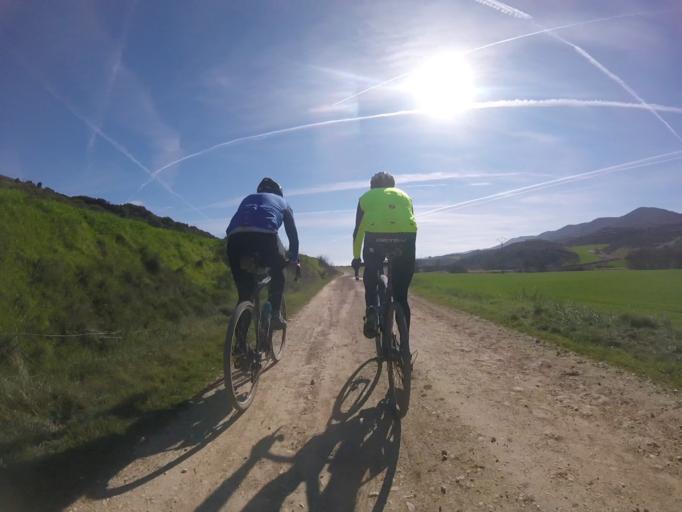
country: ES
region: Navarre
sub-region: Provincia de Navarra
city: Cirauqui
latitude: 42.6666
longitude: -1.9030
